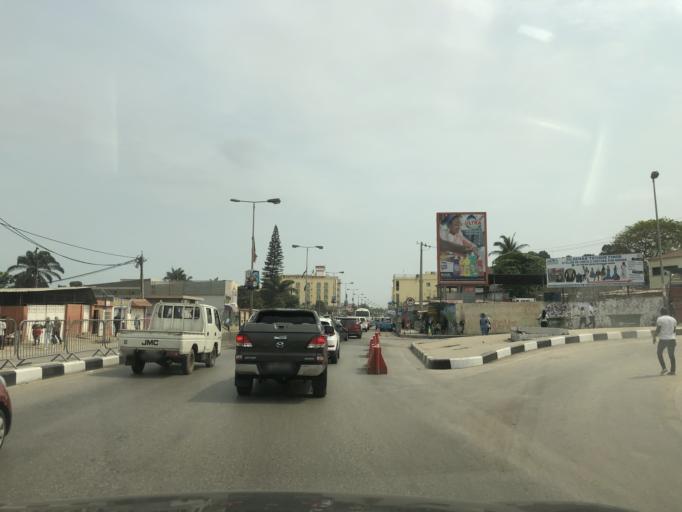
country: AO
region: Luanda
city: Luanda
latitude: -8.8451
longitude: 13.2124
